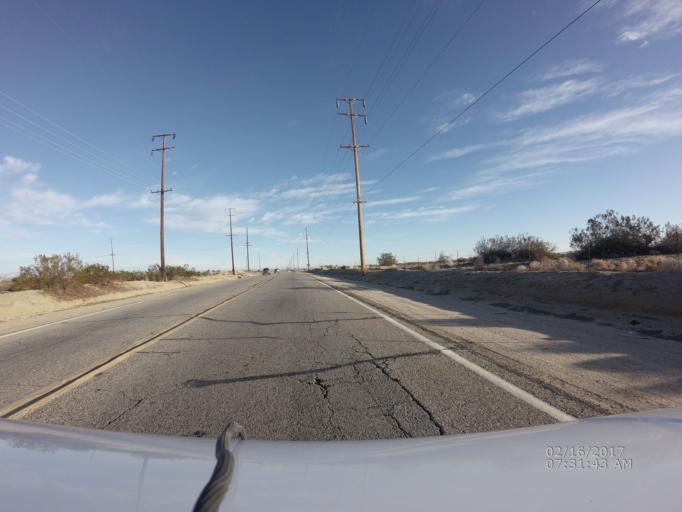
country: US
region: California
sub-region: Los Angeles County
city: Littlerock
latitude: 34.6302
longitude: -117.9696
